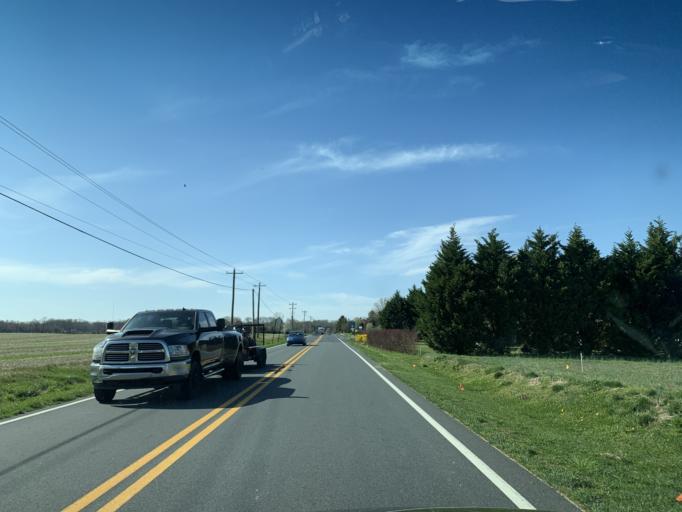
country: US
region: Delaware
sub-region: Kent County
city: Riverview
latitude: 38.9809
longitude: -75.5035
